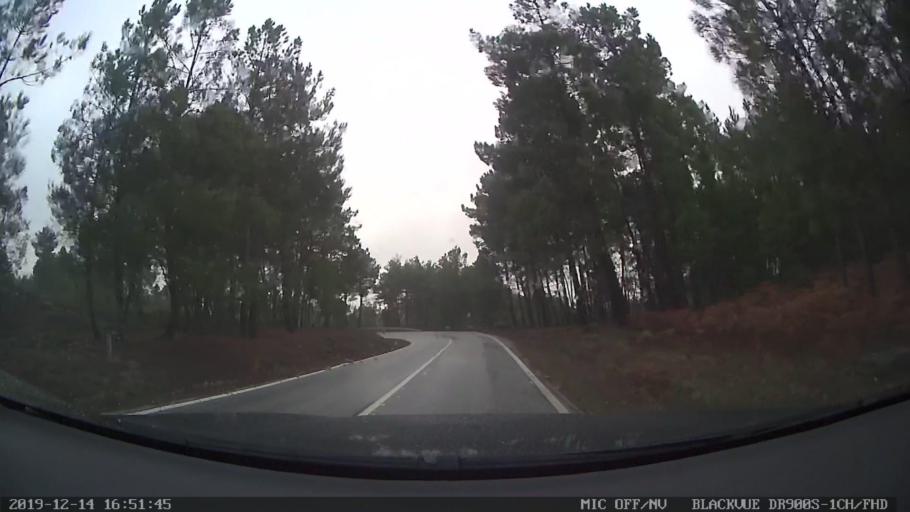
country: PT
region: Vila Real
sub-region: Murca
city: Murca
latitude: 41.4254
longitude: -7.5044
